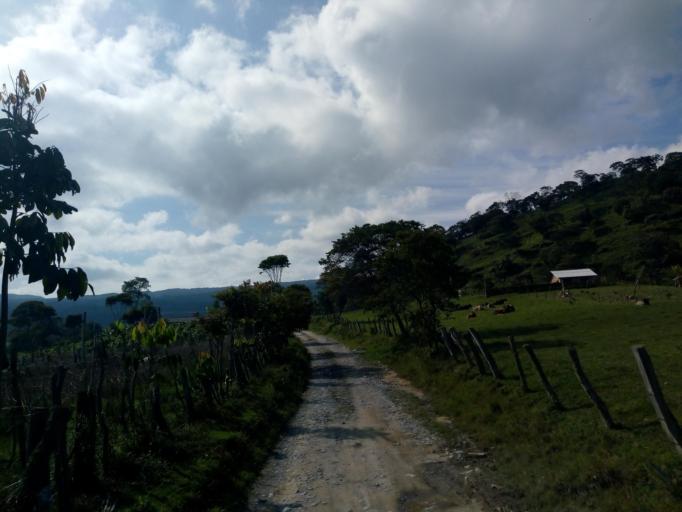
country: CO
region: Boyaca
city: Moniquira
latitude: 5.8768
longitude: -73.5067
